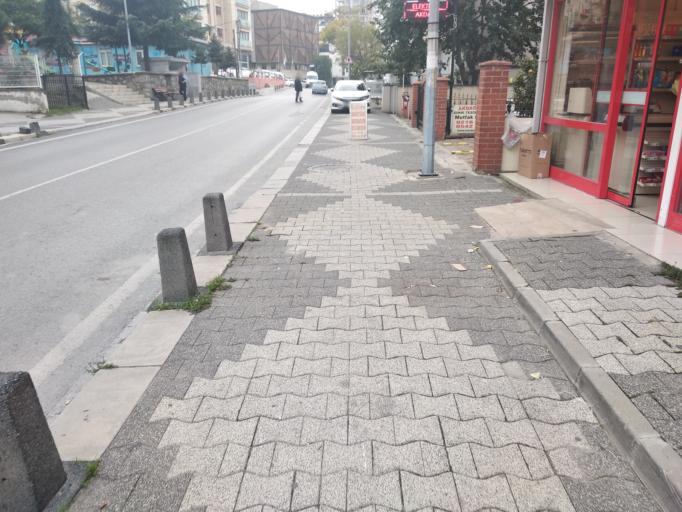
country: TR
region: Istanbul
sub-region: Atasehir
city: Atasehir
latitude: 40.9819
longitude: 29.1153
